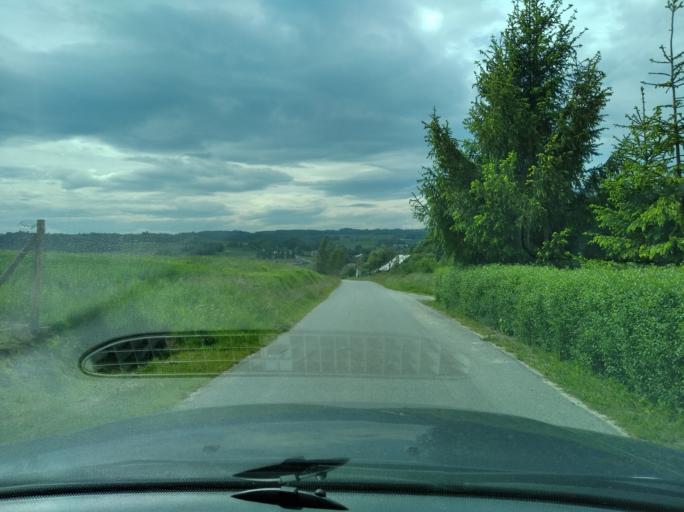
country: PL
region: Subcarpathian Voivodeship
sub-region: Powiat strzyzowski
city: Wisniowa
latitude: 49.9086
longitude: 21.6888
